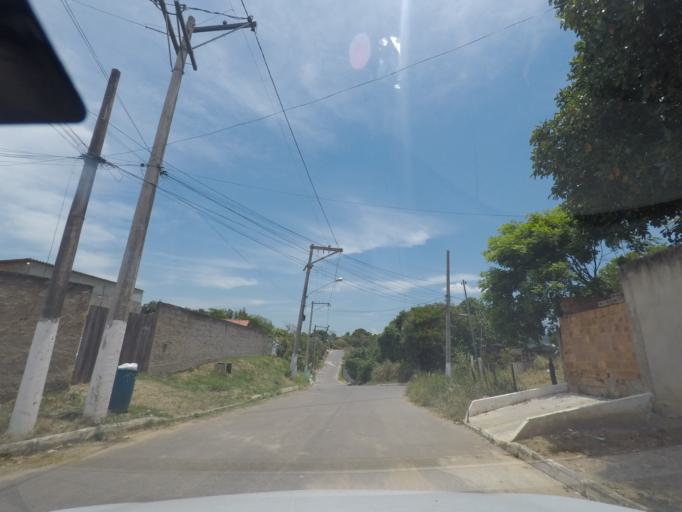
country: BR
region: Rio de Janeiro
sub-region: Marica
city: Marica
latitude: -22.9309
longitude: -42.8252
